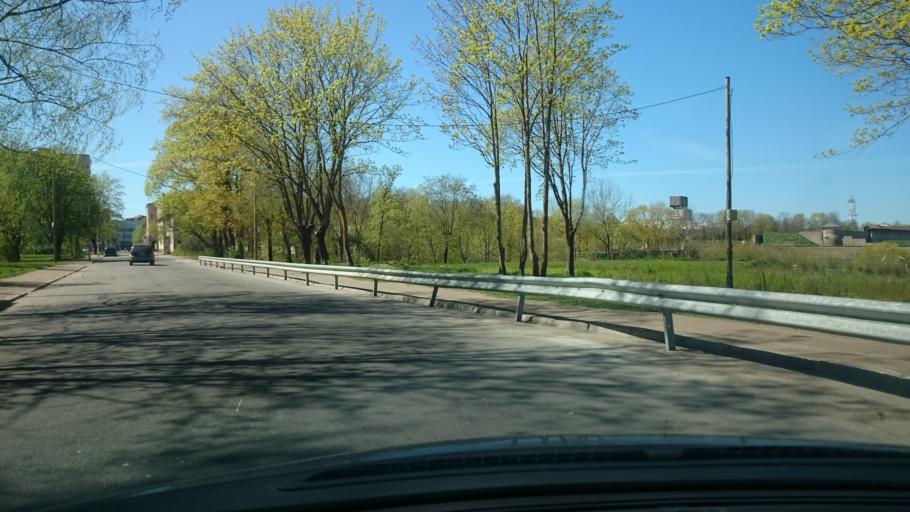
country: RU
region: Leningrad
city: Ivangorod
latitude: 59.3716
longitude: 28.2033
